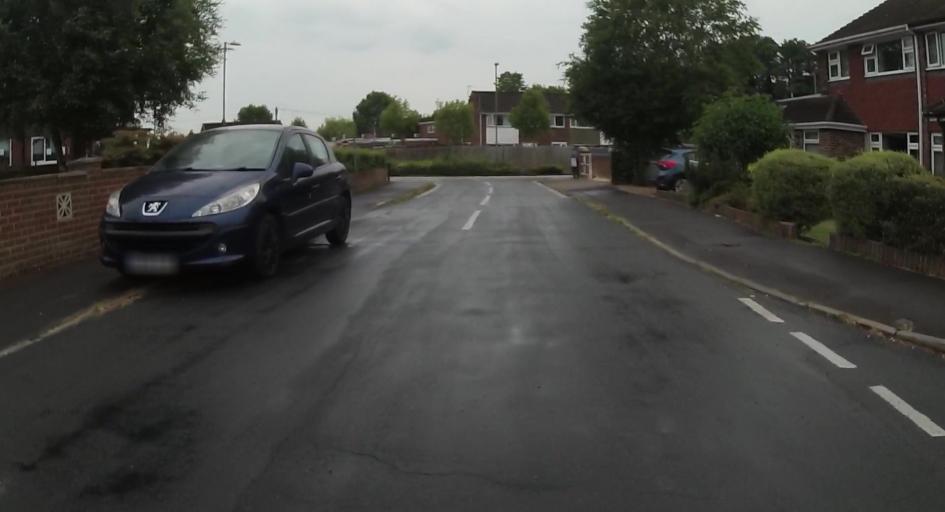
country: GB
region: England
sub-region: Hampshire
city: Farnborough
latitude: 51.2944
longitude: -0.7714
